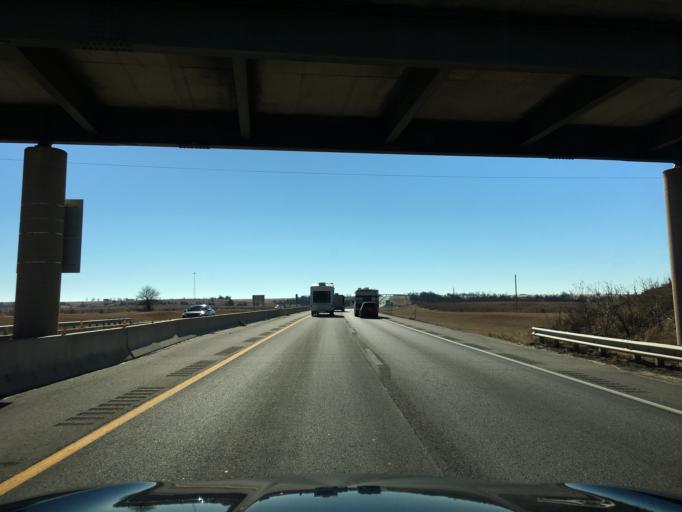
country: US
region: Oklahoma
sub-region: Kay County
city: Blackwell
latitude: 37.0141
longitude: -97.3384
